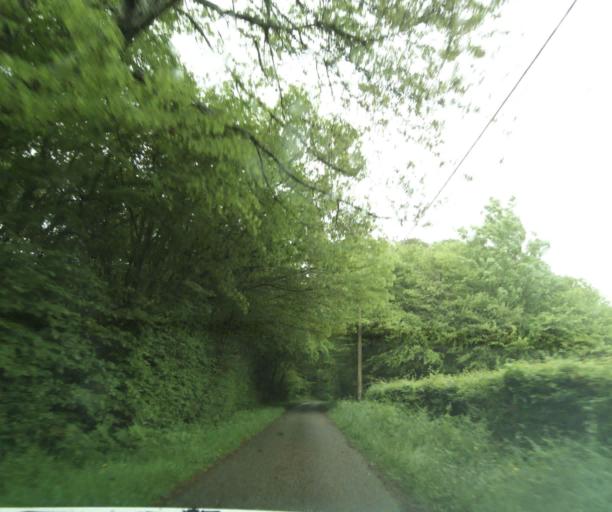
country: FR
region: Bourgogne
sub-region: Departement de Saone-et-Loire
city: Charolles
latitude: 46.5057
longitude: 4.2951
